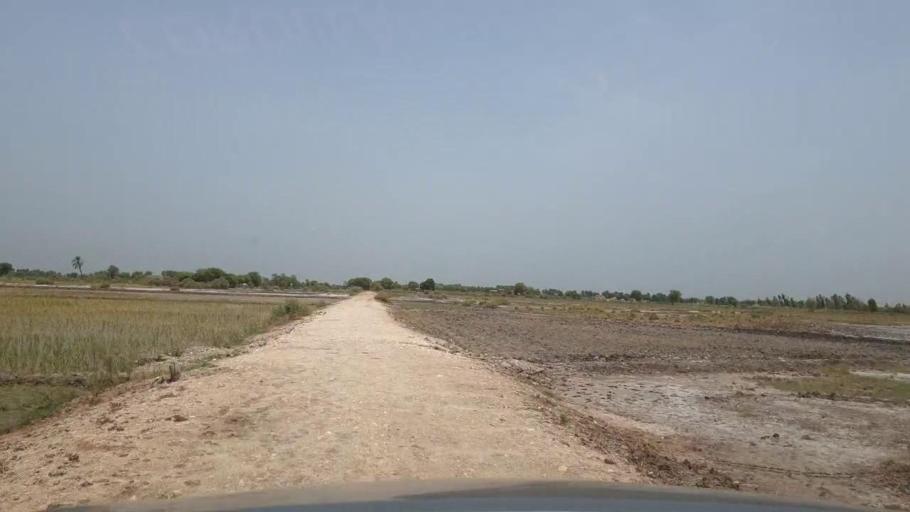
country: PK
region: Sindh
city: Madeji
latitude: 27.7630
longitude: 68.3782
